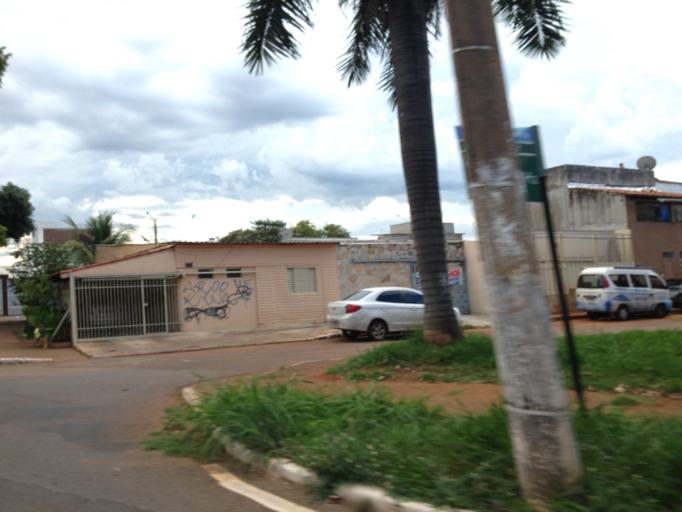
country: BR
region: Federal District
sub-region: Brasilia
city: Brasilia
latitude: -15.7813
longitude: -47.9355
